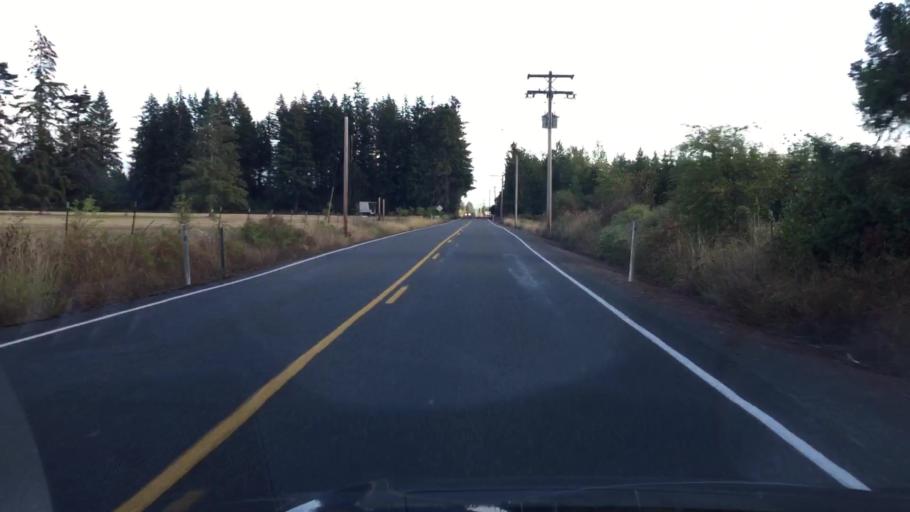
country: US
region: Washington
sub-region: Lewis County
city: Napavine
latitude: 46.5312
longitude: -122.7405
